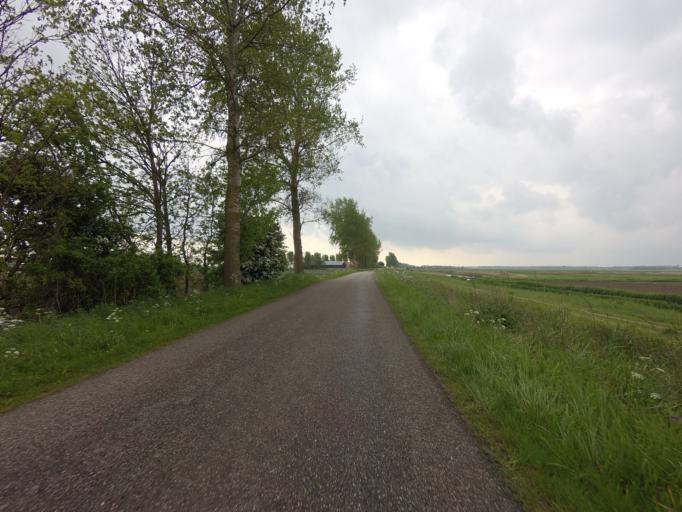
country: NL
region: South Holland
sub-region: Gemeente Goeree-Overflakkee
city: Middelharnis
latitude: 51.7193
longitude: 4.2353
